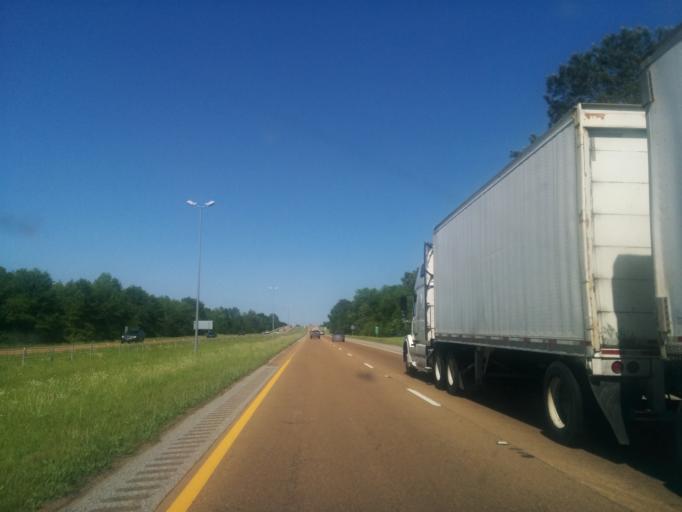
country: US
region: Mississippi
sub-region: Hinds County
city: Jackson
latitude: 32.3637
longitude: -90.2295
